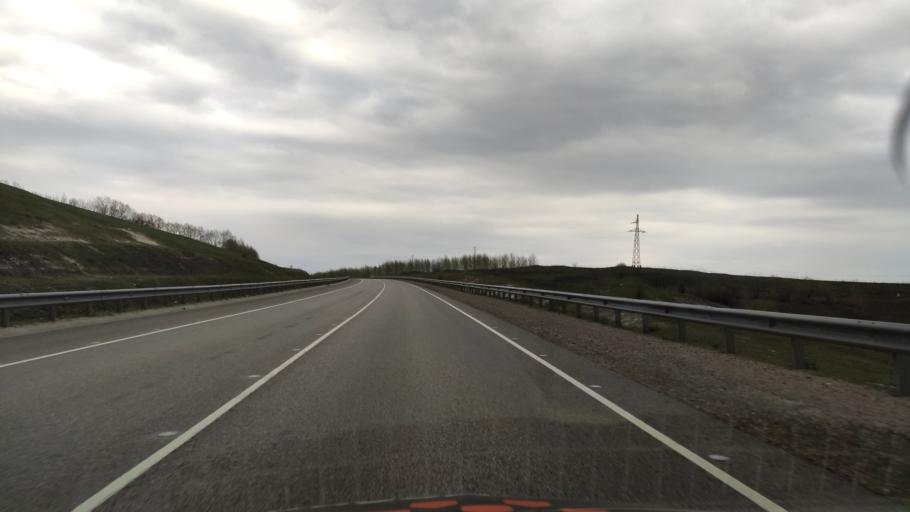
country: RU
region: Voronezj
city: Nizhnedevitsk
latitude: 51.5632
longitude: 38.4210
